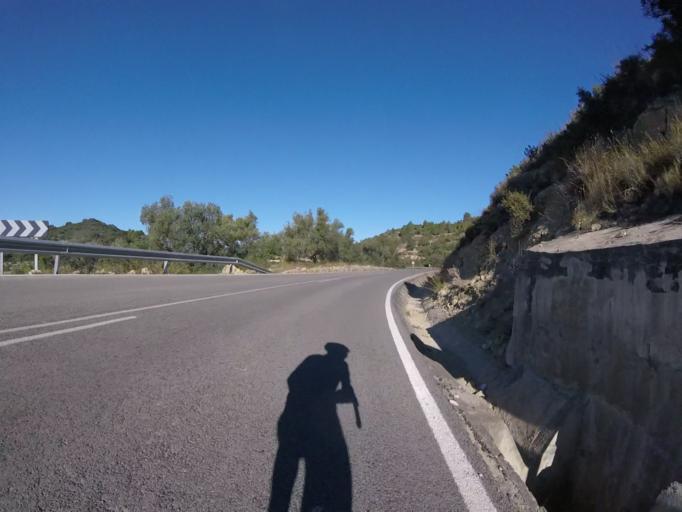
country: ES
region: Valencia
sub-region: Provincia de Castello
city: Cervera del Maestre
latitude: 40.4568
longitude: 0.2662
